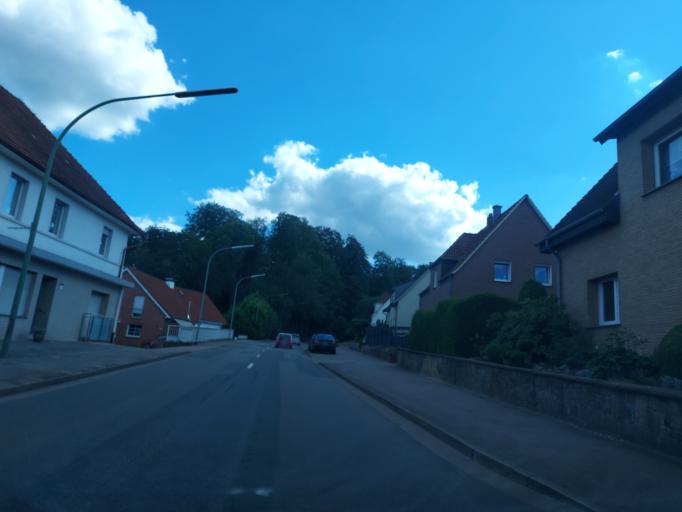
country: DE
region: Lower Saxony
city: Hagen
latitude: 52.2166
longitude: 8.0034
